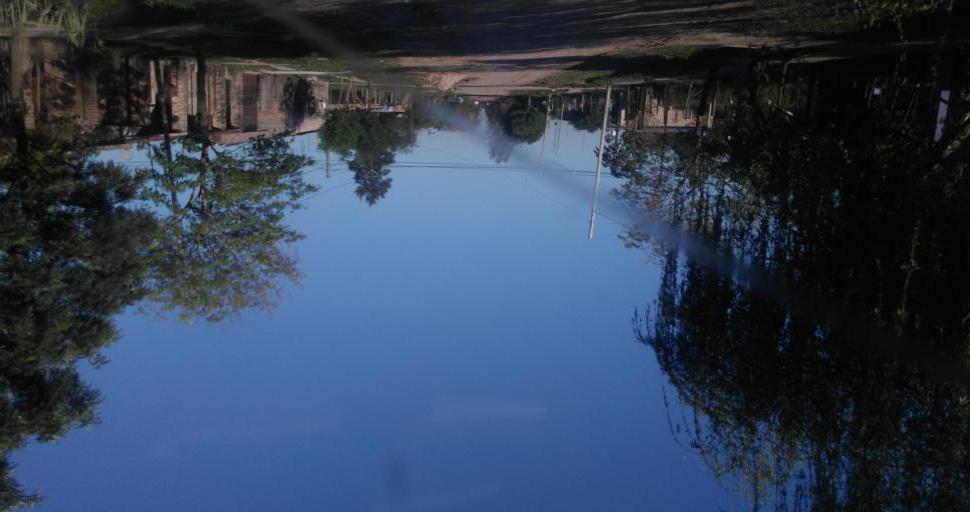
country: AR
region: Chaco
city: Resistencia
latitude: -27.4826
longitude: -59.0003
